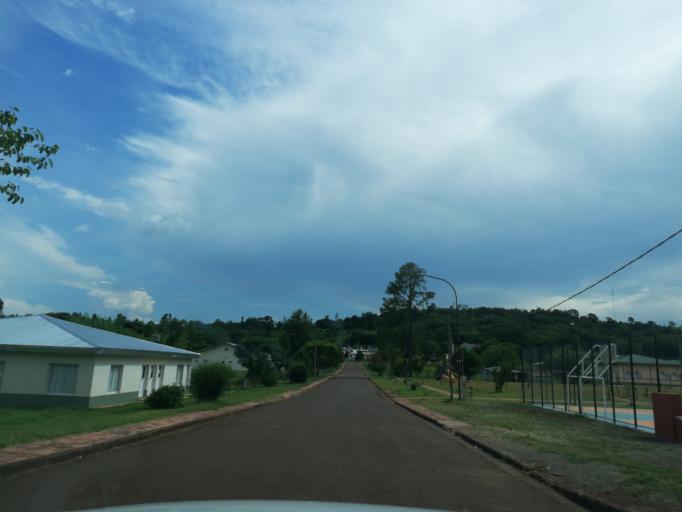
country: AR
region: Misiones
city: Cerro Azul
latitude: -27.5689
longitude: -55.5012
